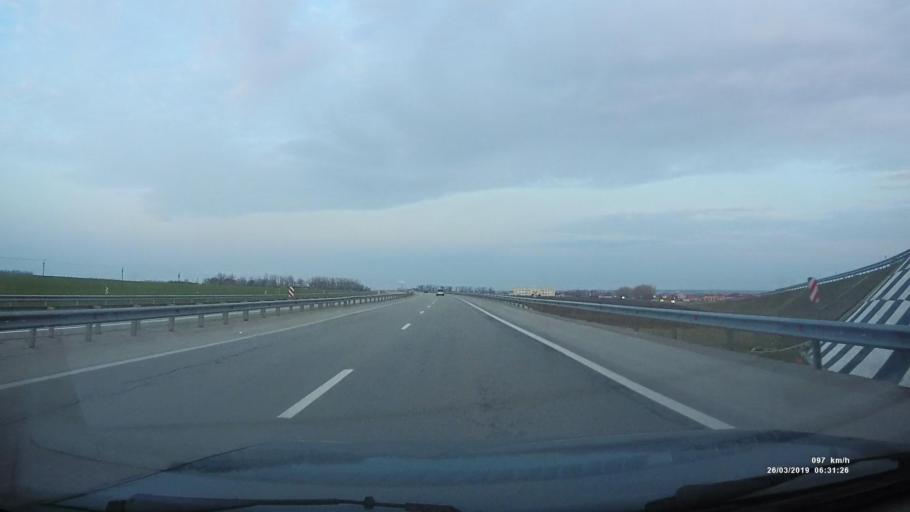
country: RU
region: Rostov
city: Krym
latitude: 47.2734
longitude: 39.5318
